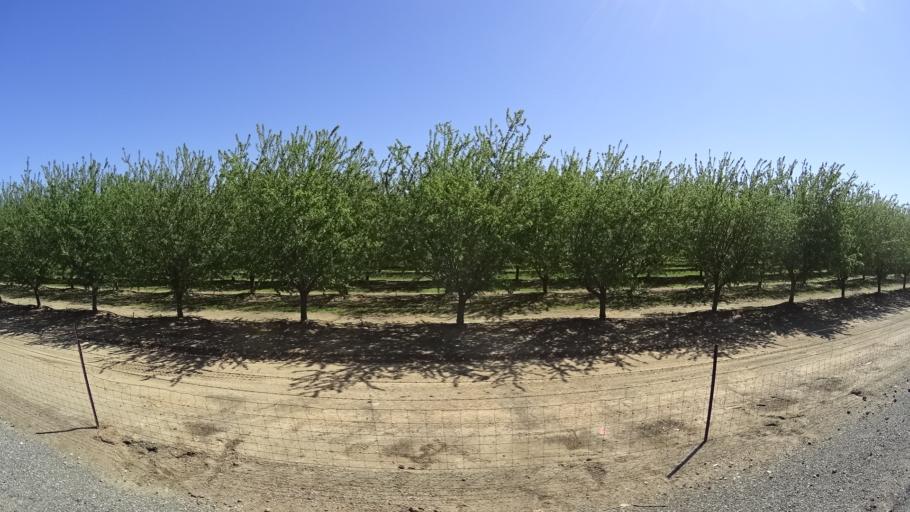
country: US
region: California
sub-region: Glenn County
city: Orland
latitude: 39.6501
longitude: -122.2533
